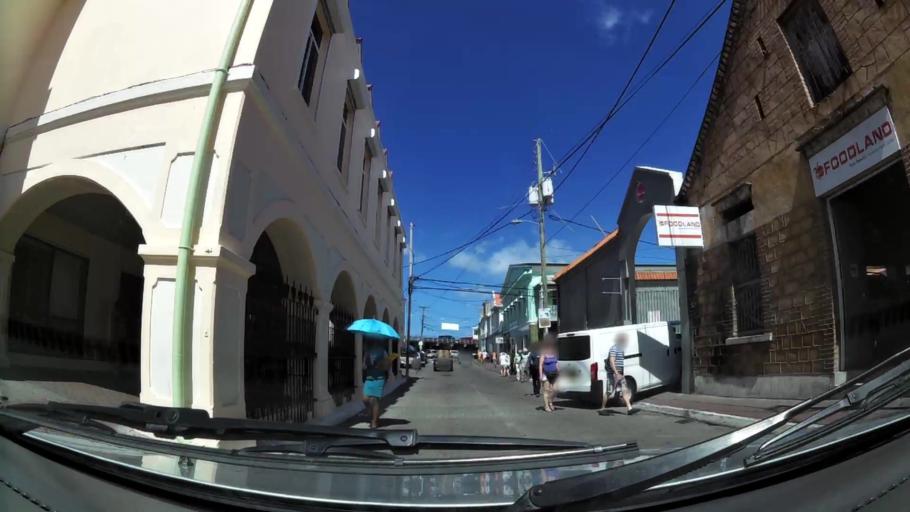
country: GD
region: Saint George
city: Saint George's
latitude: 12.0524
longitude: -61.7545
